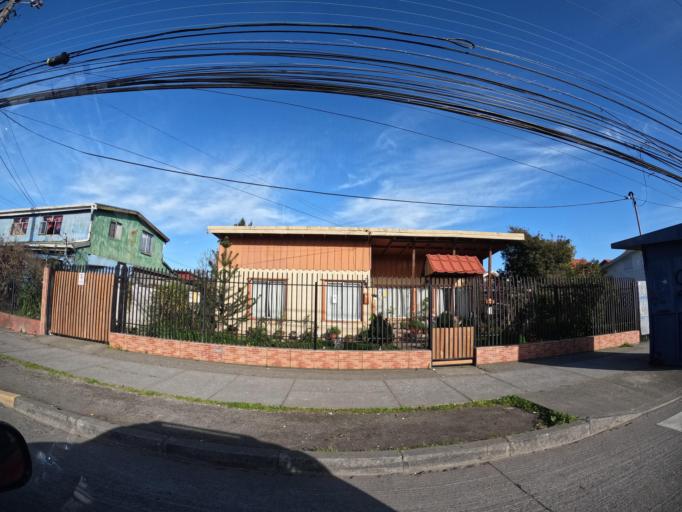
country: CL
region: Biobio
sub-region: Provincia de Concepcion
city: Talcahuano
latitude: -36.7470
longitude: -73.0926
